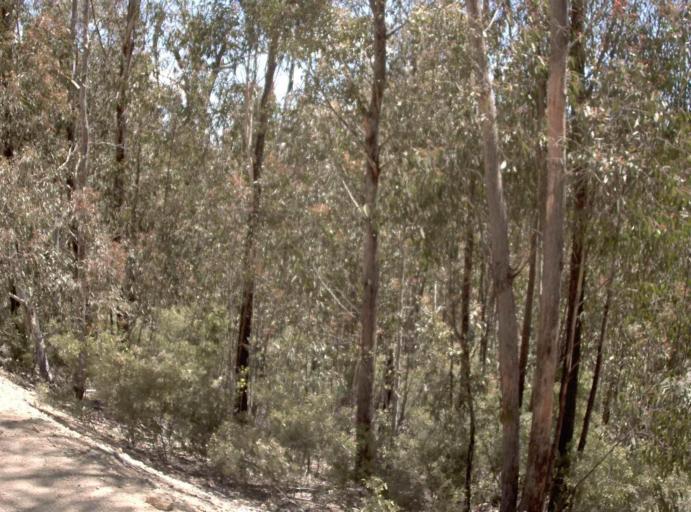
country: AU
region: New South Wales
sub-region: Snowy River
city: Jindabyne
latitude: -37.0779
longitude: 148.3289
